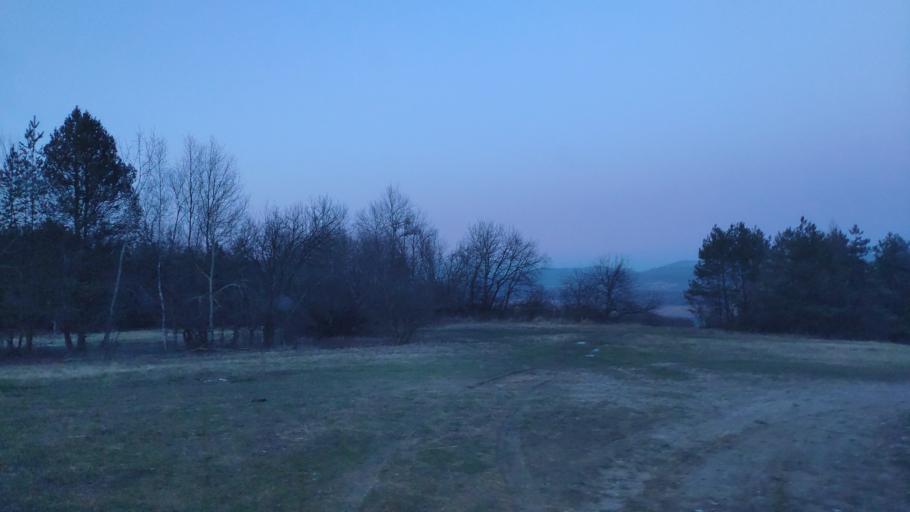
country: SK
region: Kosicky
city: Kosice
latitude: 48.8344
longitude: 21.2535
